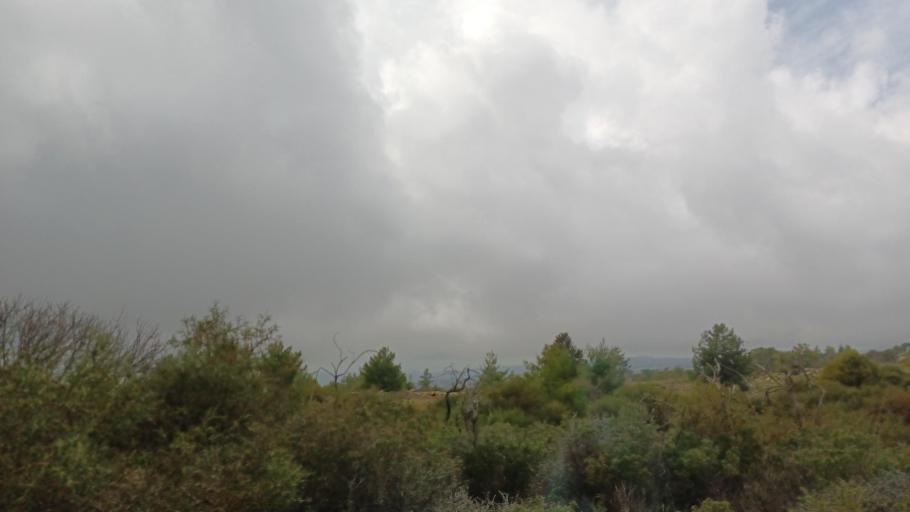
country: CY
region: Limassol
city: Pachna
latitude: 34.7659
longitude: 32.8293
